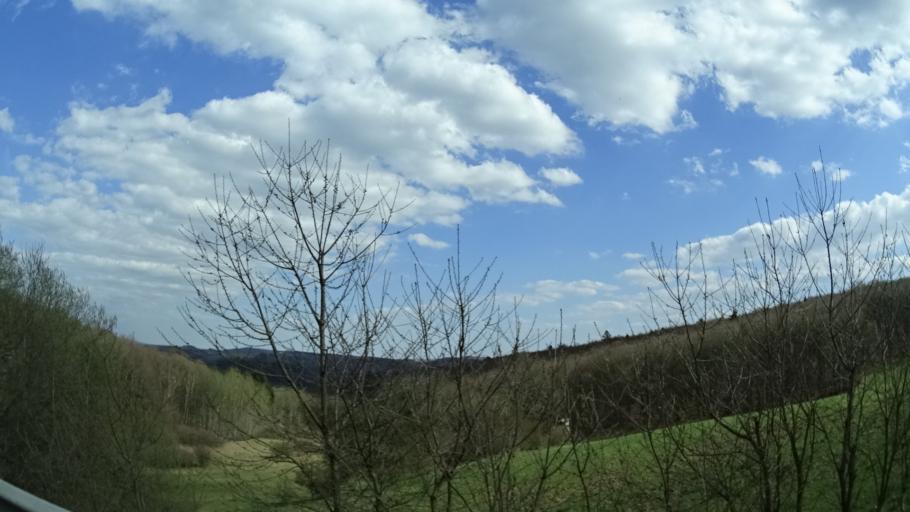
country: DE
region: Rheinland-Pfalz
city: Herborn
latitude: 49.7683
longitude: 7.2996
